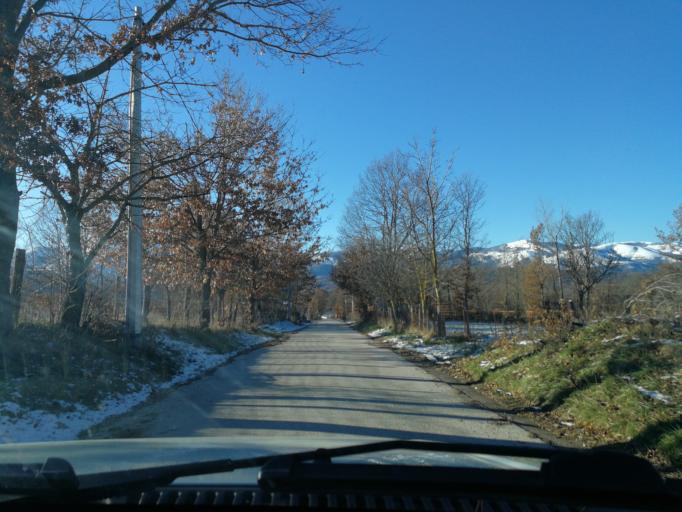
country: IT
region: Latium
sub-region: Provincia di Rieti
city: Amatrice
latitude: 42.6556
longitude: 13.2947
